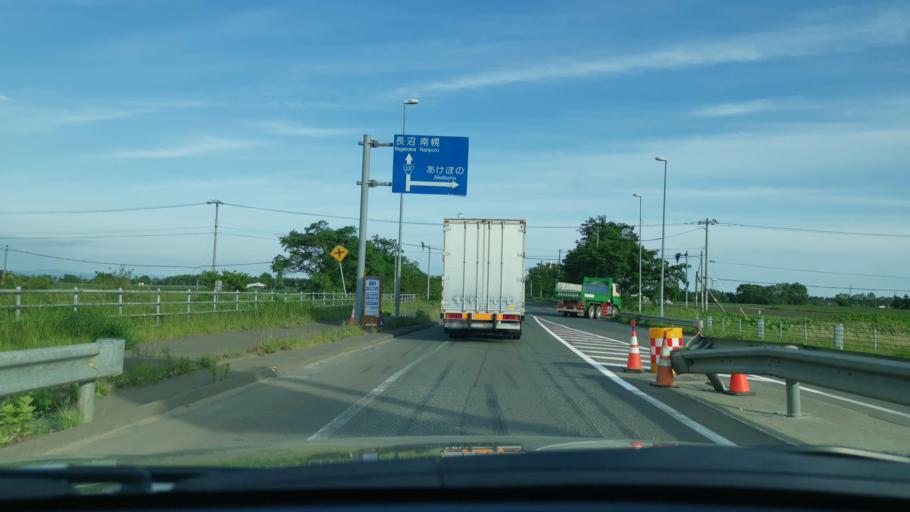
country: JP
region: Hokkaido
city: Ebetsu
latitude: 43.1124
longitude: 141.5893
